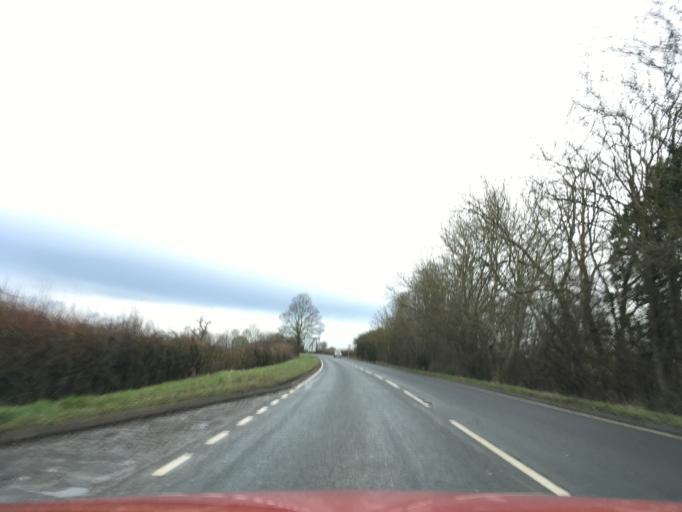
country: GB
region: England
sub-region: Worcestershire
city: Evesham
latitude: 52.0518
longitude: -1.9613
